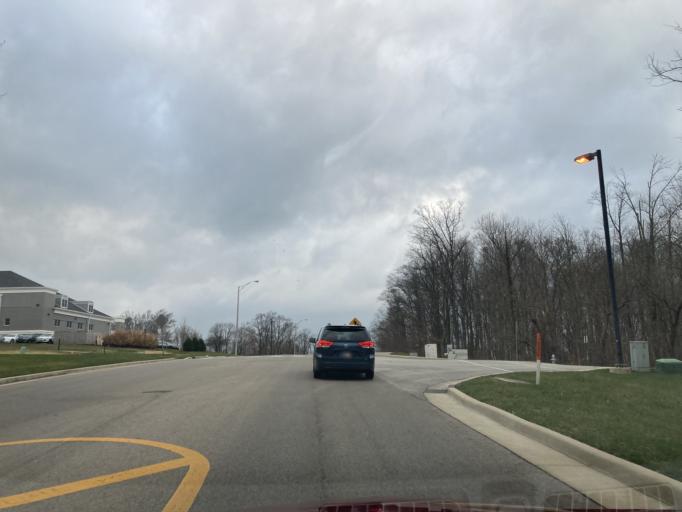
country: US
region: Indiana
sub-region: Monroe County
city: Bloomington
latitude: 39.1789
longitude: -86.5106
